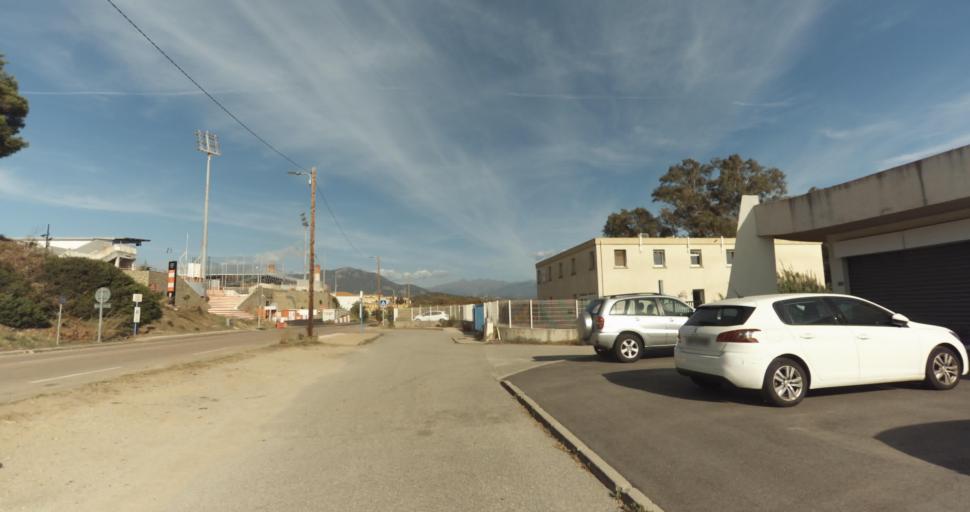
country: FR
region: Corsica
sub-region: Departement de la Corse-du-Sud
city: Ajaccio
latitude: 41.9297
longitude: 8.7752
